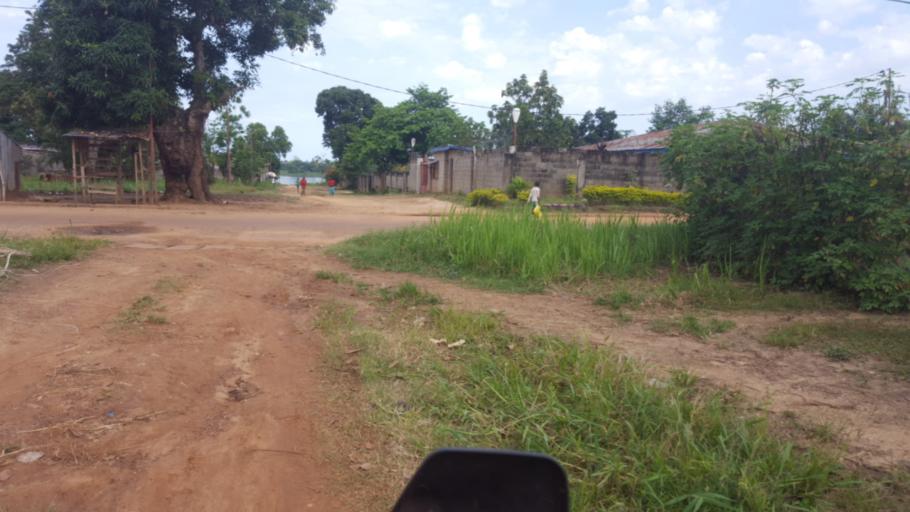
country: CD
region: Bandundu
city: Bandundu
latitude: -3.3022
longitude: 17.3716
